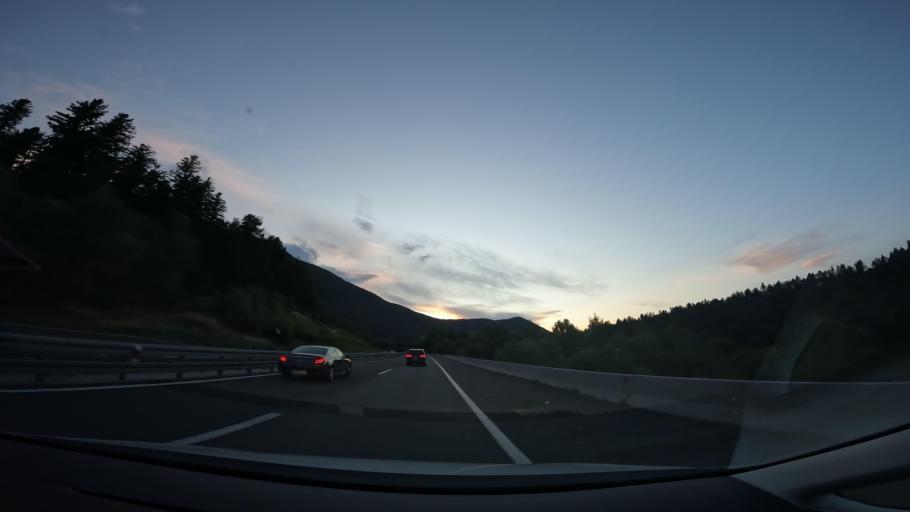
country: HR
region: Primorsko-Goranska
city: Hreljin
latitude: 45.3196
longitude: 14.6741
